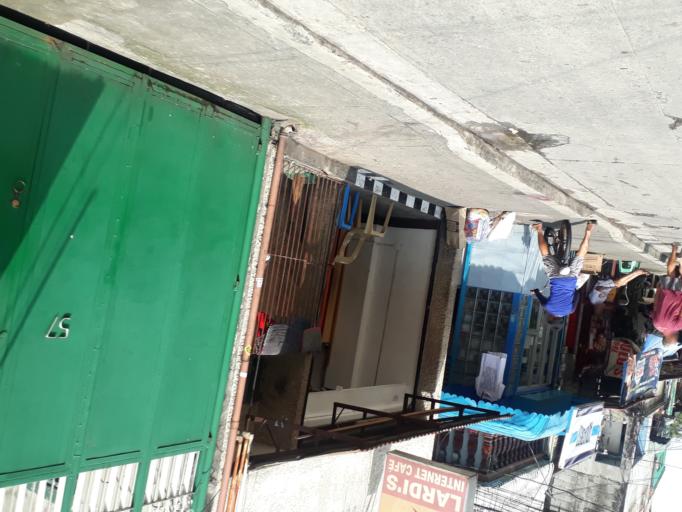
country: PH
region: Metro Manila
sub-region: San Juan
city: San Juan
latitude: 14.6165
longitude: 121.0496
